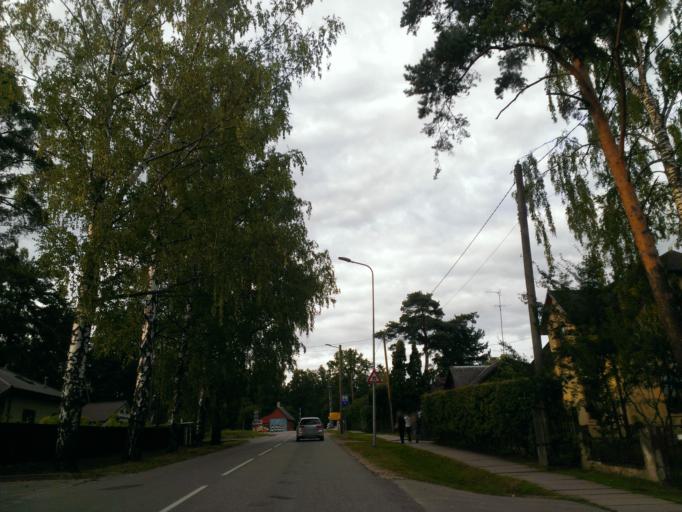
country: LV
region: Ogre
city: Ogre
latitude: 56.8207
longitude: 24.5814
